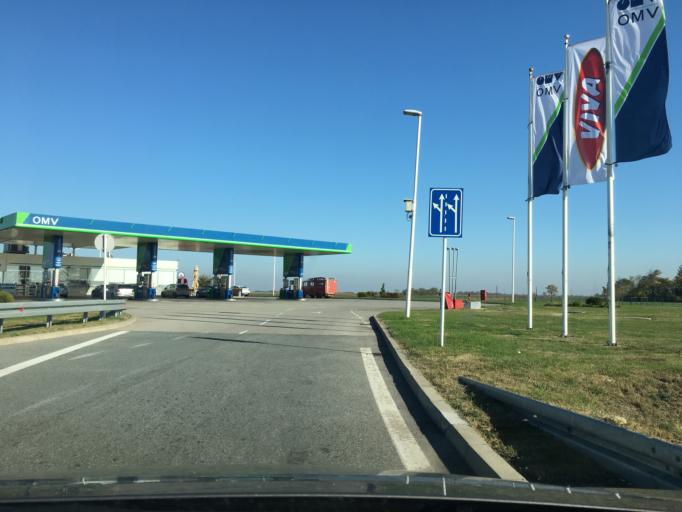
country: RS
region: Autonomna Pokrajina Vojvodina
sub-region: Severnobacki Okrug
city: Backa Topola
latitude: 45.7940
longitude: 19.6940
